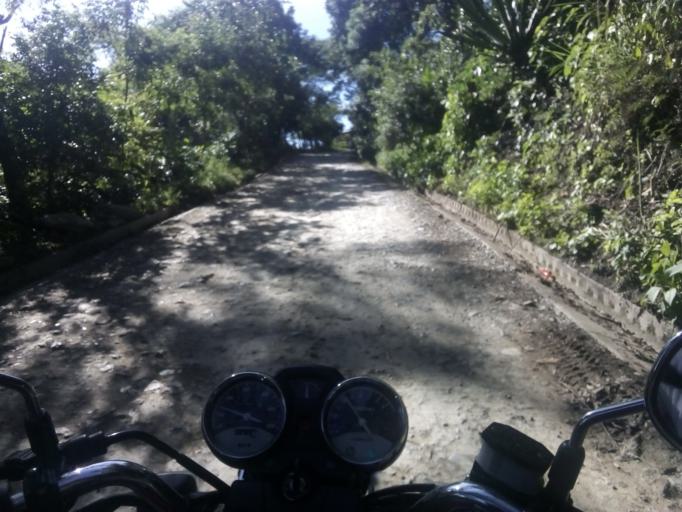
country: CO
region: Santander
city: Guepsa
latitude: 6.0107
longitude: -73.5463
